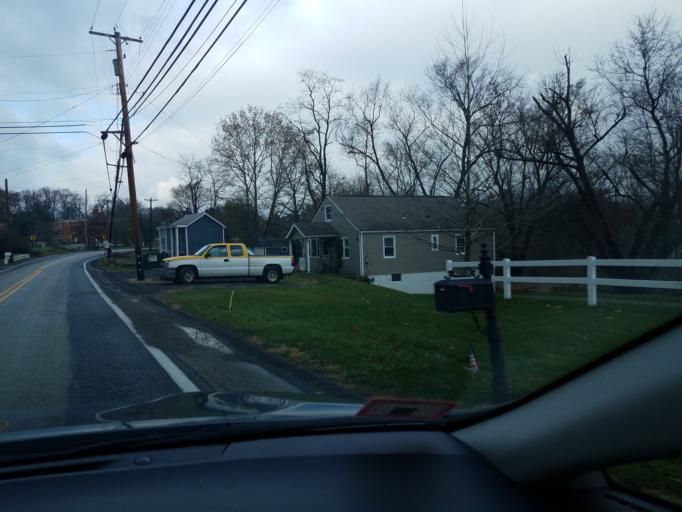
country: US
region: Pennsylvania
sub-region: Allegheny County
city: Franklin Park
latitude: 40.5861
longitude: -80.0935
